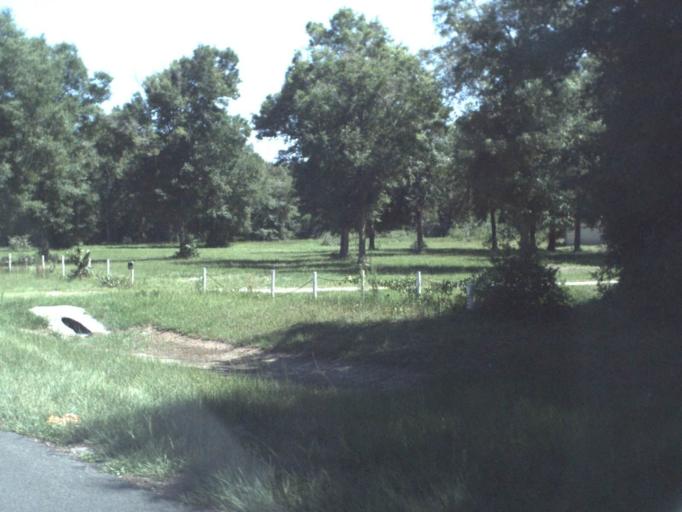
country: US
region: Florida
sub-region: Lafayette County
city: Mayo
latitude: 30.1175
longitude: -83.2607
